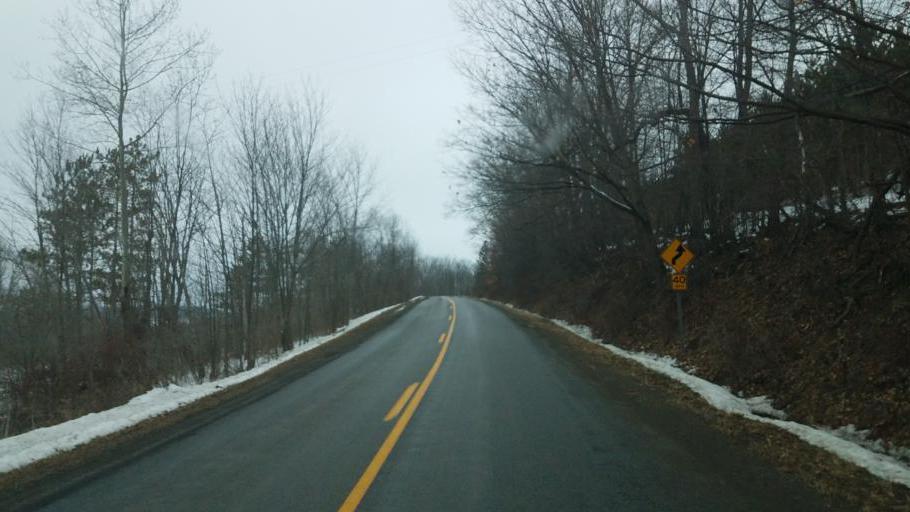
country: US
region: Pennsylvania
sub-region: Tioga County
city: Westfield
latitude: 42.0804
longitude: -77.4726
